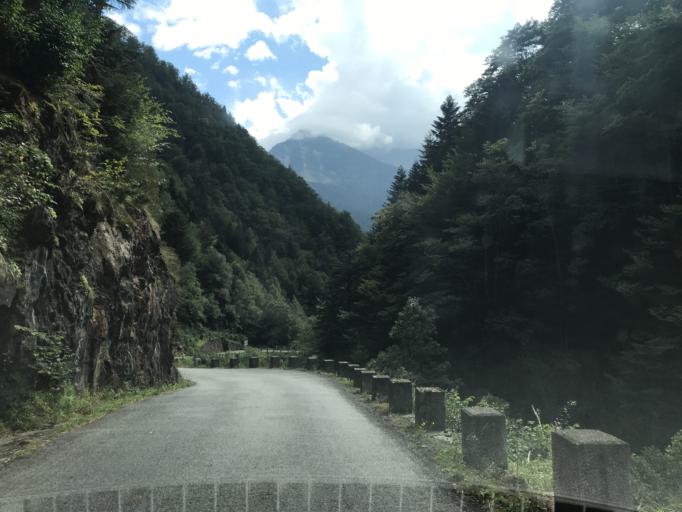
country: FR
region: Midi-Pyrenees
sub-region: Departement des Hautes-Pyrenees
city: Saint-Lary-Soulan
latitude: 42.8004
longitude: 0.2299
